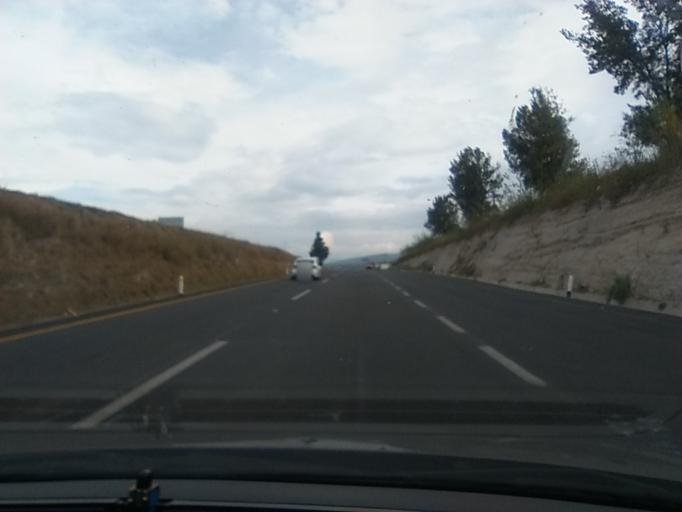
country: MX
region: Michoacan
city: Vistahermosa de Negrete
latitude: 20.2716
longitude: -102.4439
